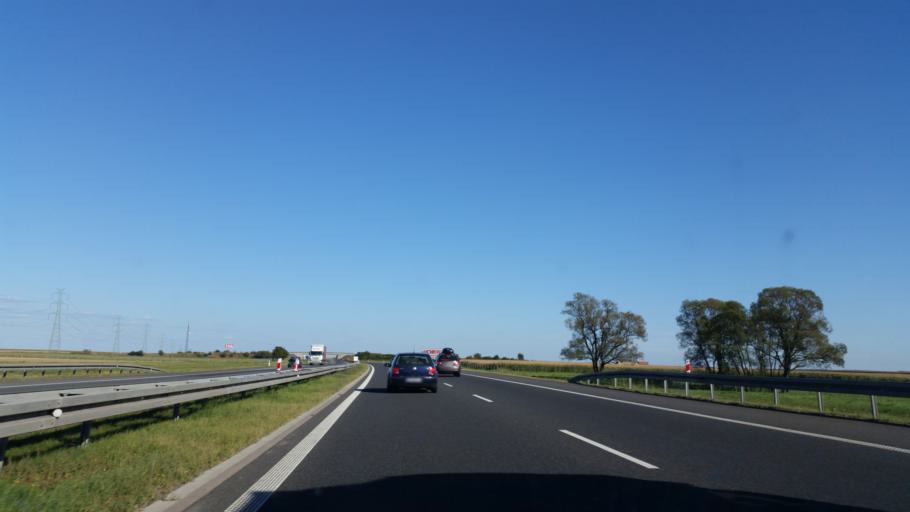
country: PL
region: Opole Voivodeship
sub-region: Powiat brzeski
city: Olszanka
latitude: 50.7406
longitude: 17.4623
